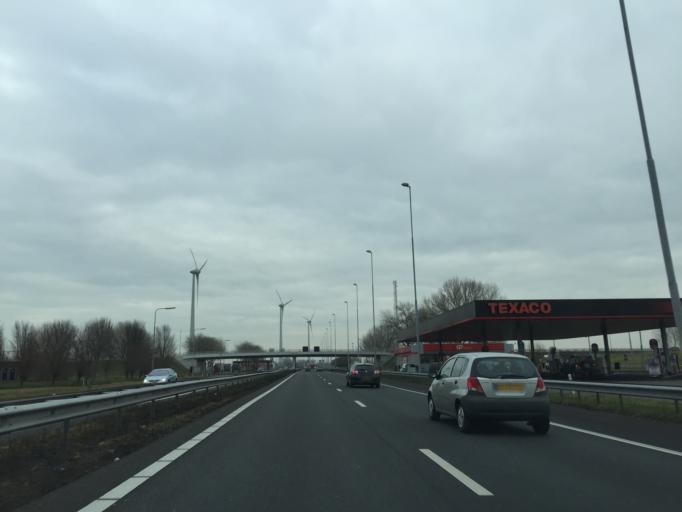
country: NL
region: South Holland
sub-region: Gemeente Hardinxveld-Giessendam
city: Boven-Hardinxveld
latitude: 51.8305
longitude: 4.8784
